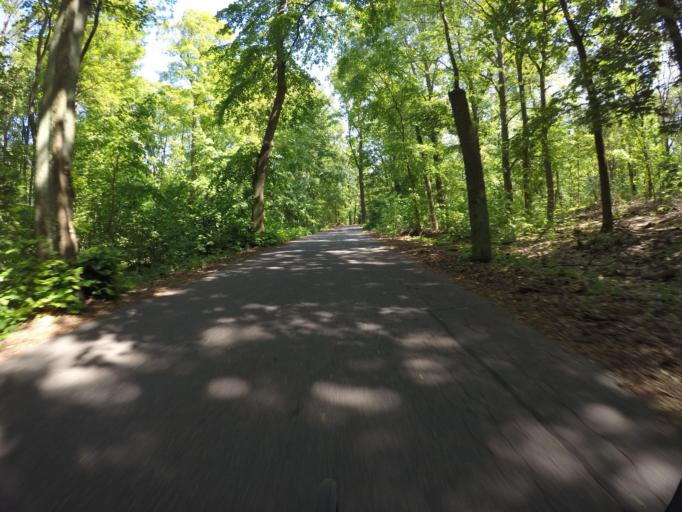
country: DE
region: Berlin
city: Wannsee
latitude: 52.4256
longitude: 13.1465
